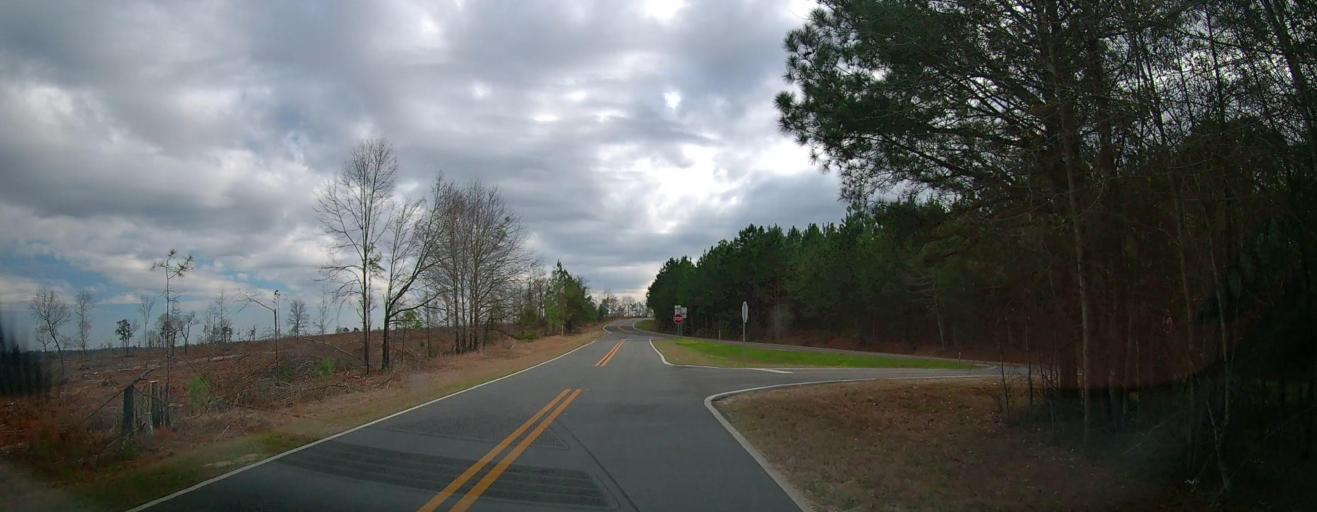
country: US
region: Georgia
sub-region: Marion County
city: Buena Vista
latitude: 32.4332
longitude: -84.4278
